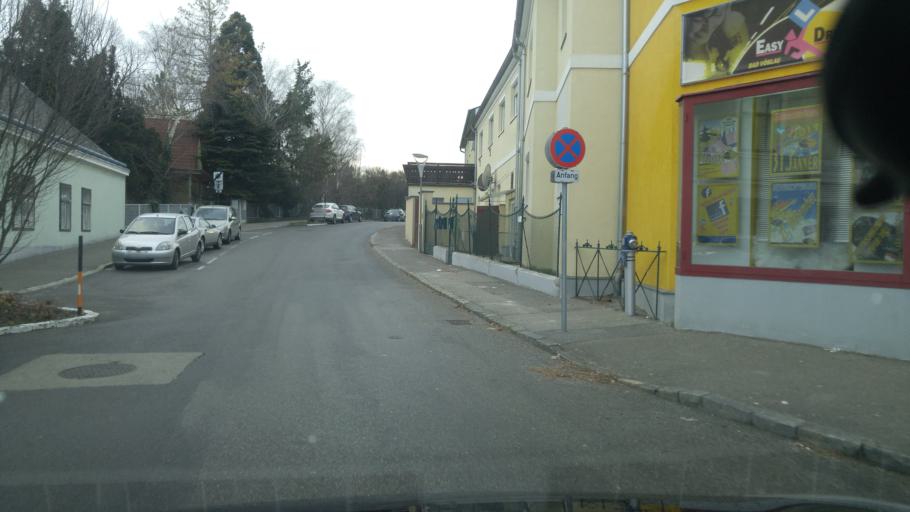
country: AT
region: Lower Austria
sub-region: Politischer Bezirk Baden
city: Bad Voslau
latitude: 47.9635
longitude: 16.2163
